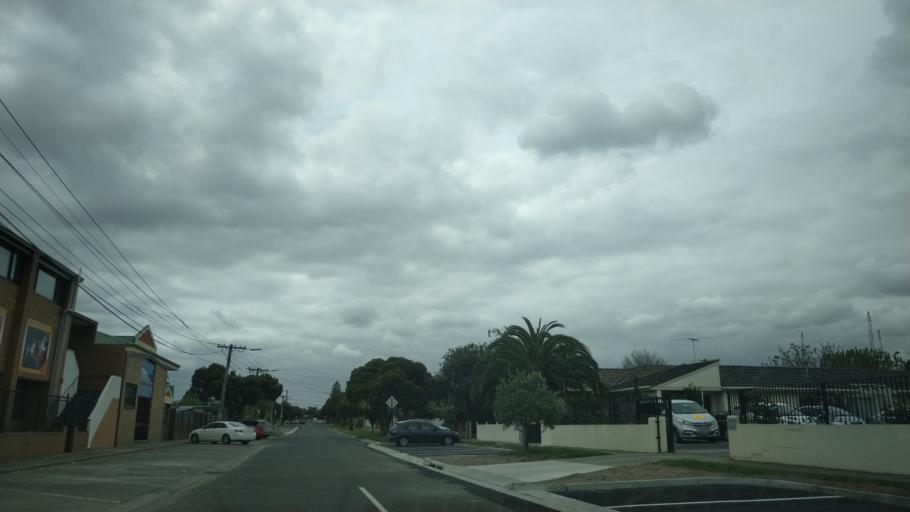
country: AU
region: Victoria
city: Hughesdale
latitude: -37.8965
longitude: 145.0833
